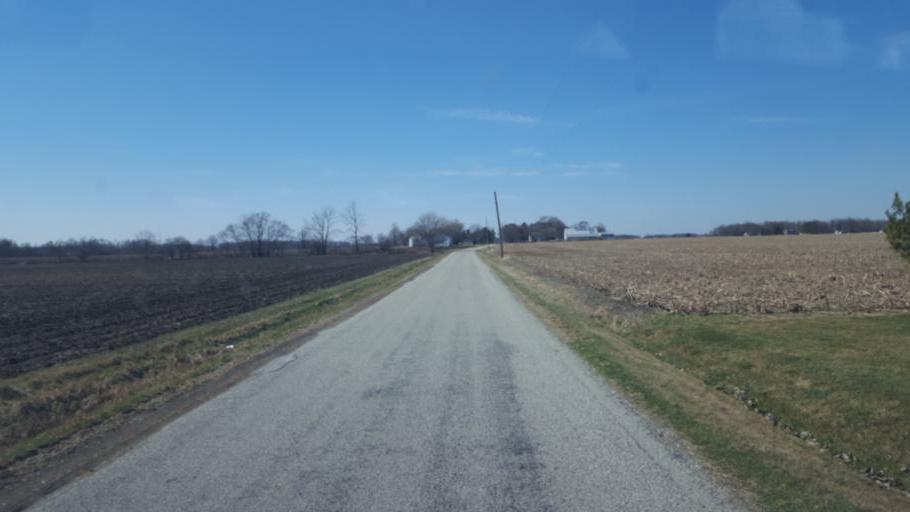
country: US
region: Ohio
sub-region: Marion County
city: Prospect
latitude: 40.4982
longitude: -83.1201
